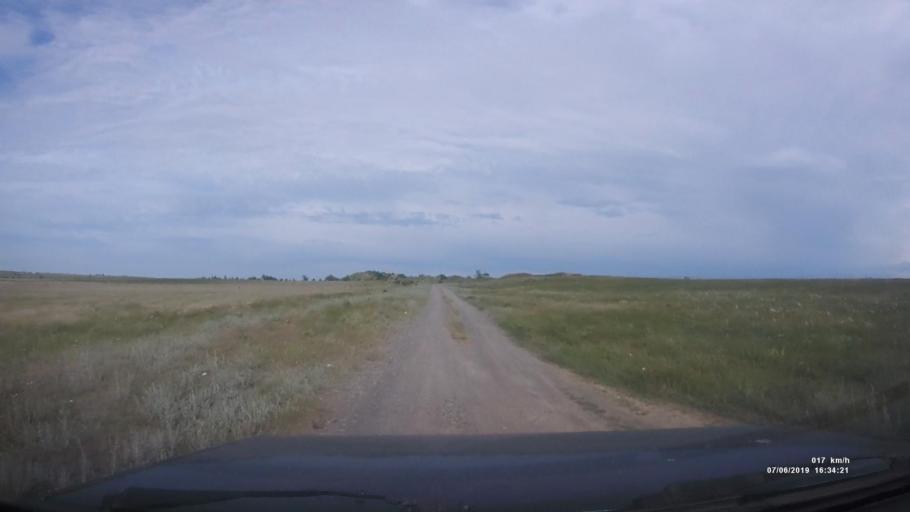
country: RU
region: Rostov
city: Staraya Stanitsa
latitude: 48.2512
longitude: 40.3408
